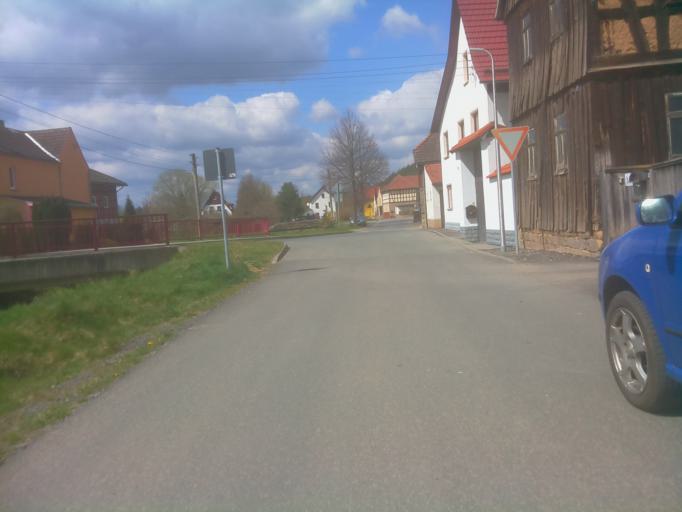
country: DE
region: Thuringia
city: Kleinebersdorf
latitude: 50.8176
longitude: 11.8372
